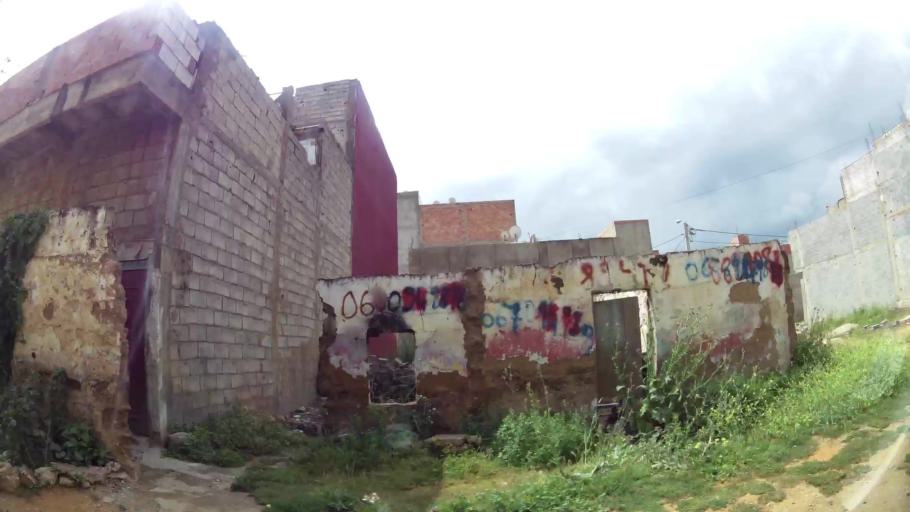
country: MA
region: Rabat-Sale-Zemmour-Zaer
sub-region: Khemisset
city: Tiflet
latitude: 33.8927
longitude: -6.3244
